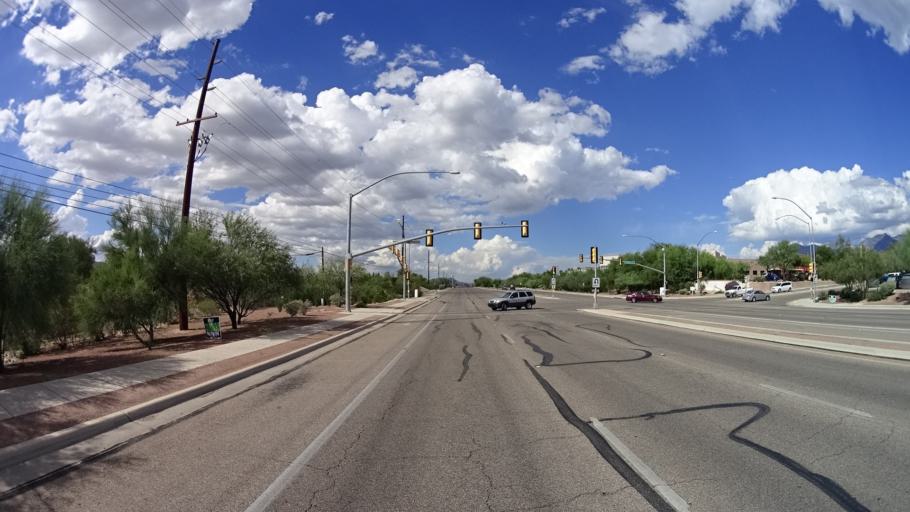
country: US
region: Arizona
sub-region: Pima County
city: Casas Adobes
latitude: 32.3154
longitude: -111.0122
